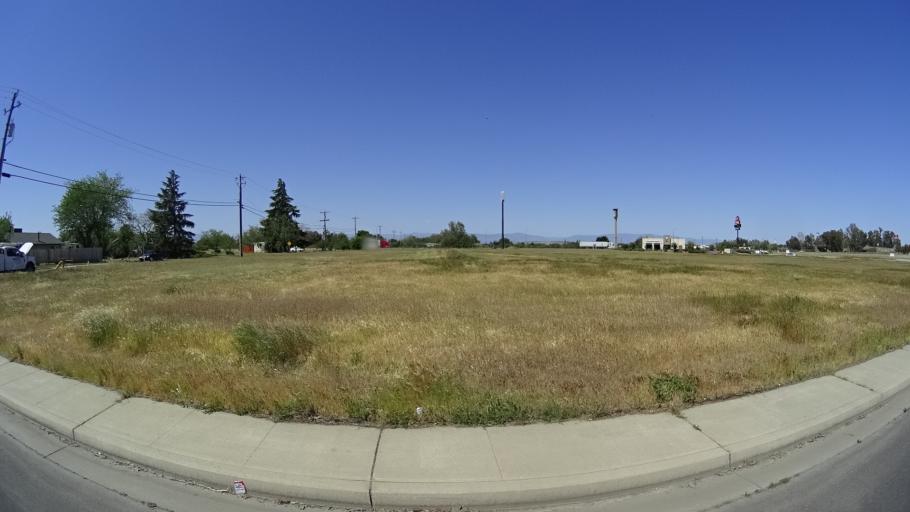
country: US
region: California
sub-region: Glenn County
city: Orland
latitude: 39.7476
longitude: -122.2026
